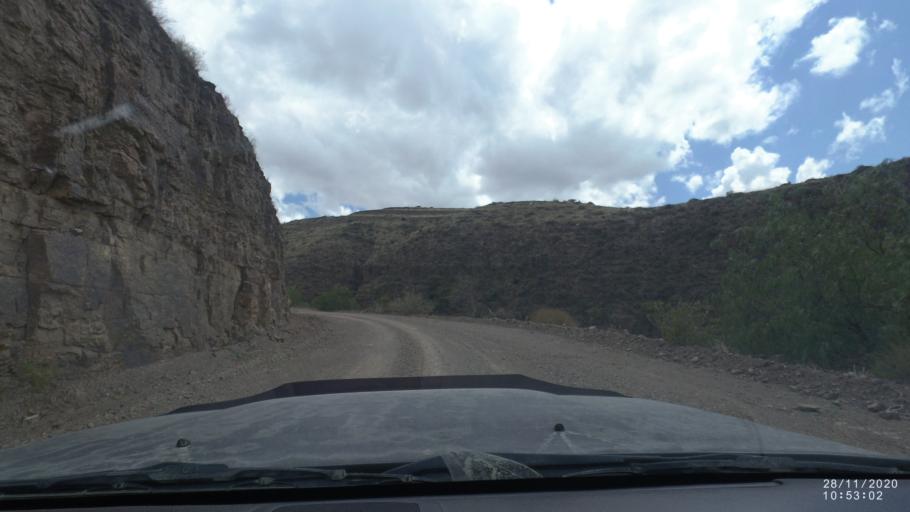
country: BO
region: Cochabamba
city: Capinota
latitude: -17.7831
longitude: -66.1186
